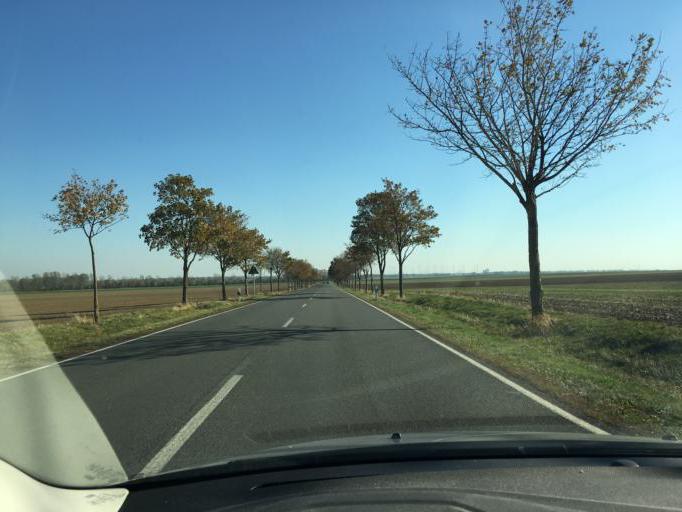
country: DE
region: Saxony-Anhalt
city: Wanzleben
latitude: 52.0330
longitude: 11.4752
